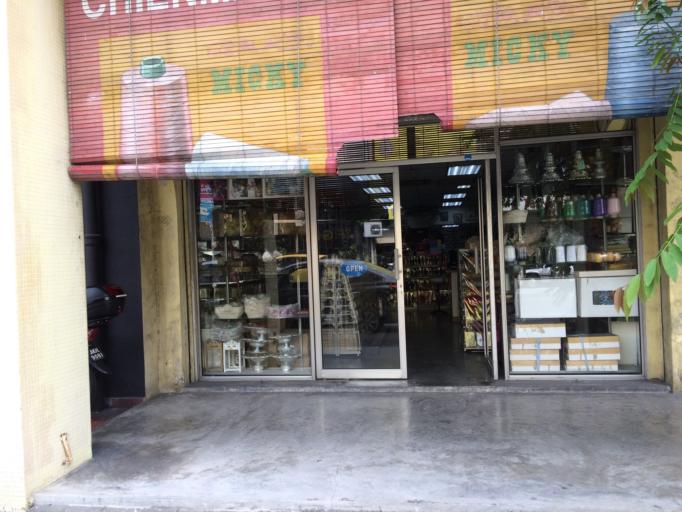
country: MY
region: Perak
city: Ipoh
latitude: 4.5937
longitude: 101.0822
